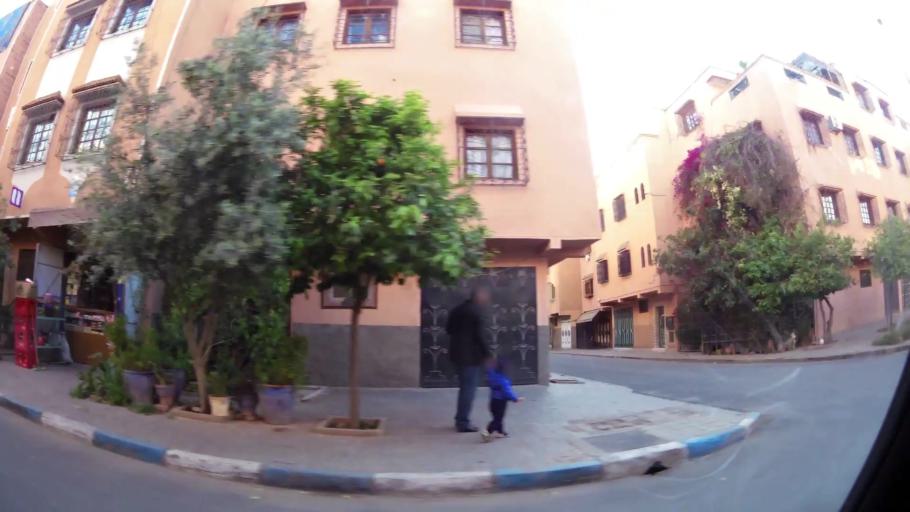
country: MA
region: Marrakech-Tensift-Al Haouz
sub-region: Marrakech
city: Marrakesh
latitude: 31.6166
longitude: -8.0555
